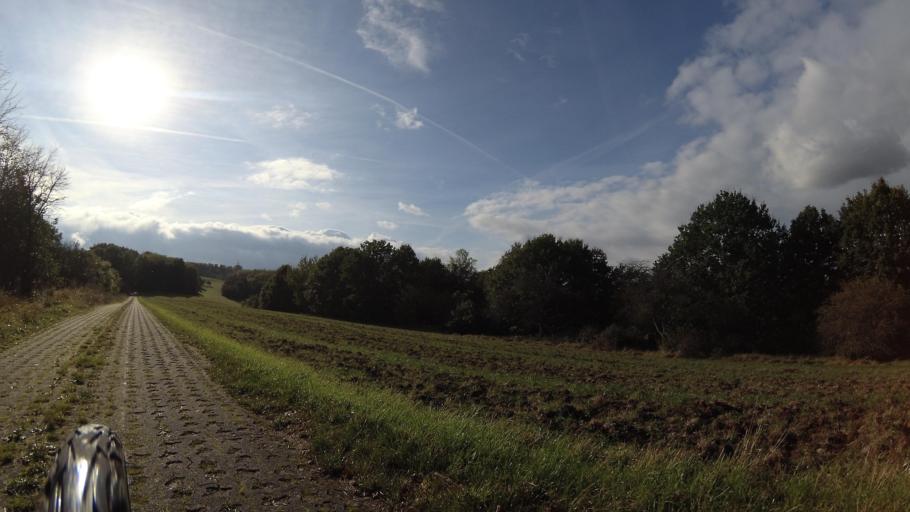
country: DE
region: Rheinland-Pfalz
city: Ohmbach
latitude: 49.4469
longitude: 7.3446
